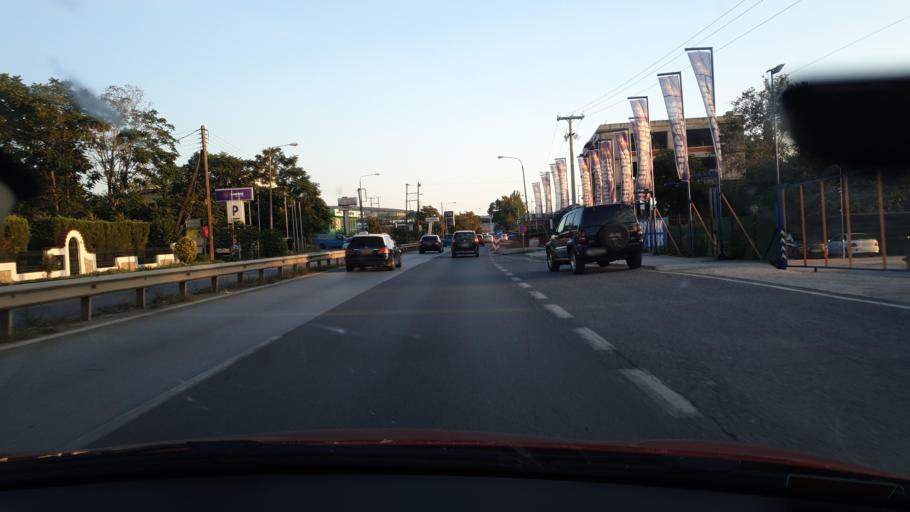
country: GR
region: Central Macedonia
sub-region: Nomos Thessalonikis
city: Thermi
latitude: 40.5300
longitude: 22.9950
